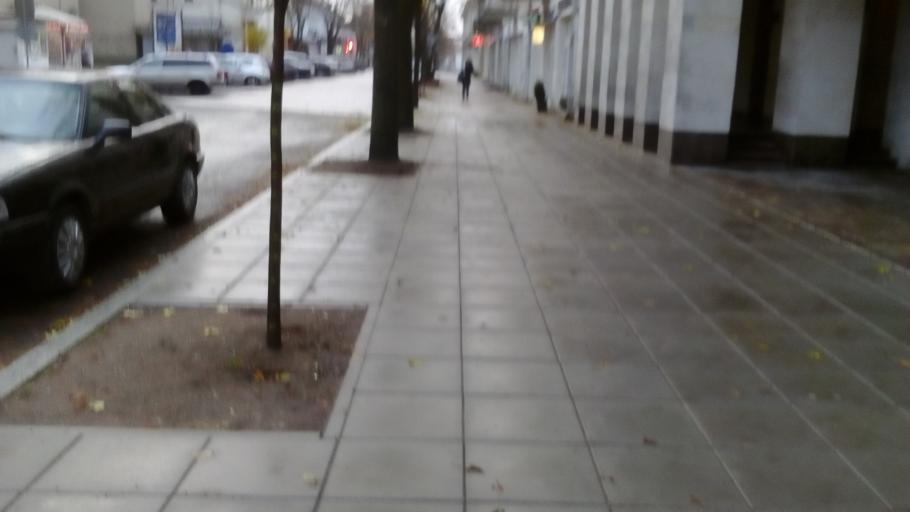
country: LT
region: Kauno apskritis
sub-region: Kaunas
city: Kaunas
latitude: 54.8969
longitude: 23.9179
